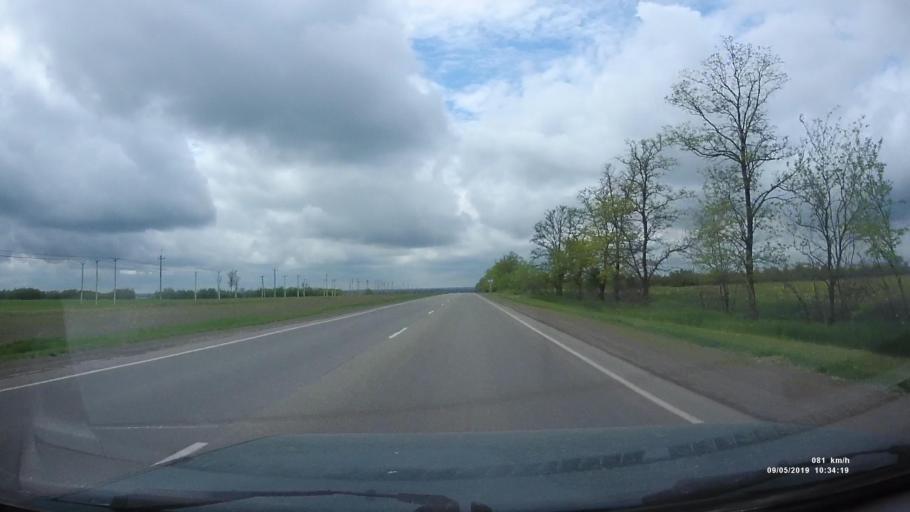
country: RU
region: Rostov
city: Peshkovo
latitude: 47.0555
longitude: 39.4205
